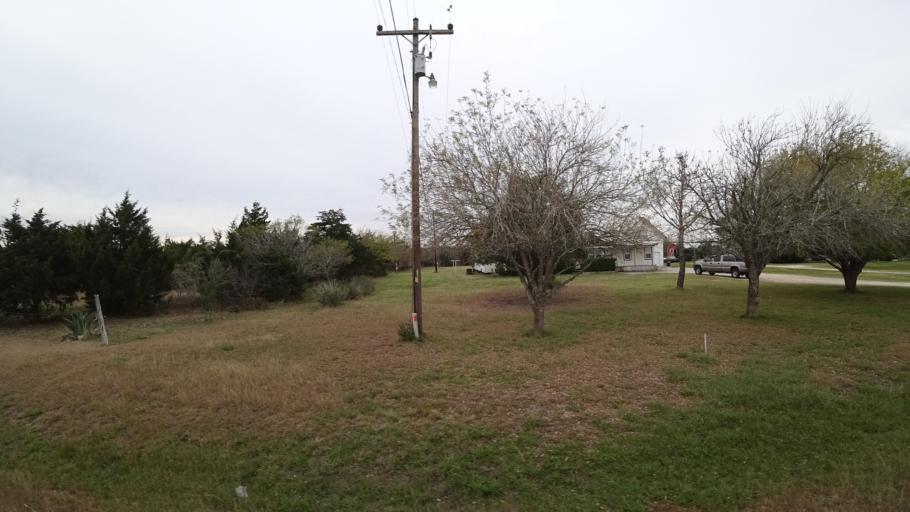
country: US
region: Texas
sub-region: Travis County
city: Garfield
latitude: 30.1092
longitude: -97.5824
